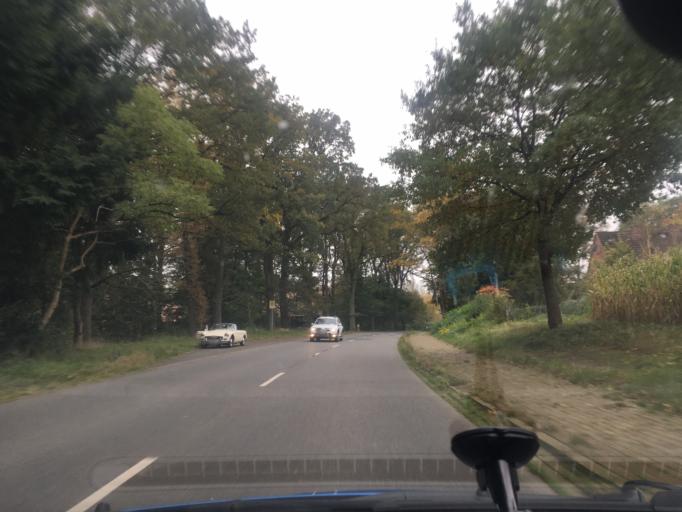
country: DE
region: Lower Saxony
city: Bispingen
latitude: 53.0300
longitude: 9.9998
